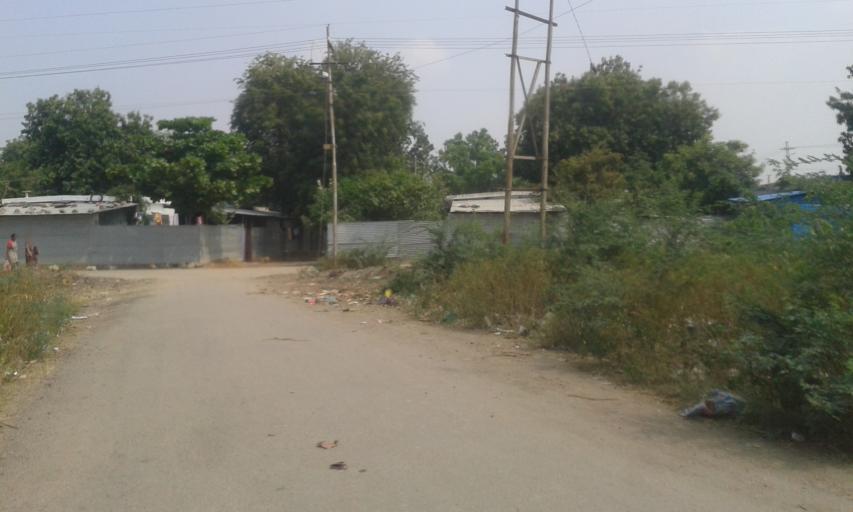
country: IN
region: Karnataka
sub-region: Raichur
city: Lingsugur
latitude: 16.1916
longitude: 76.6612
